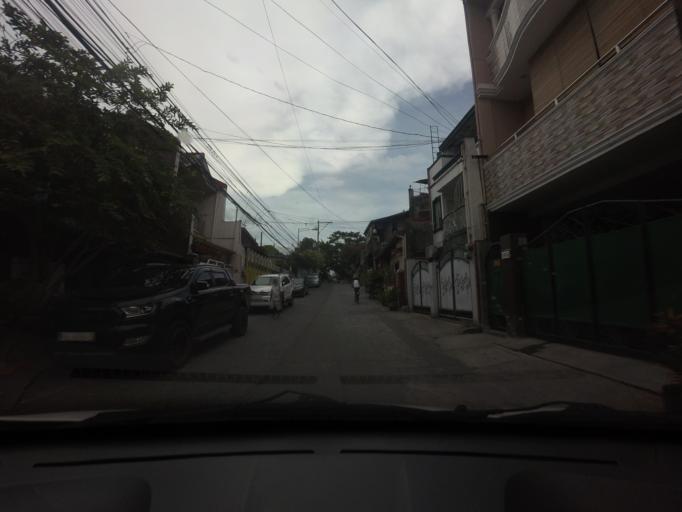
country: PH
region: Calabarzon
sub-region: Province of Rizal
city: Pateros
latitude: 14.5494
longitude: 121.0600
